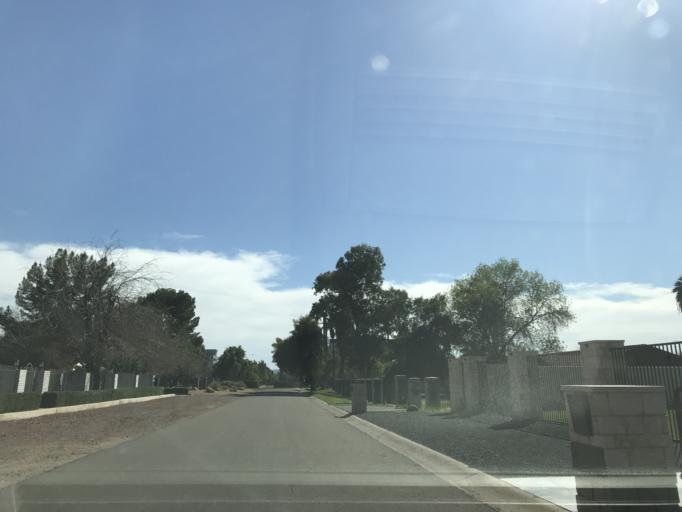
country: US
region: Arizona
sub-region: Maricopa County
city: Phoenix
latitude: 33.5120
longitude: -112.0345
